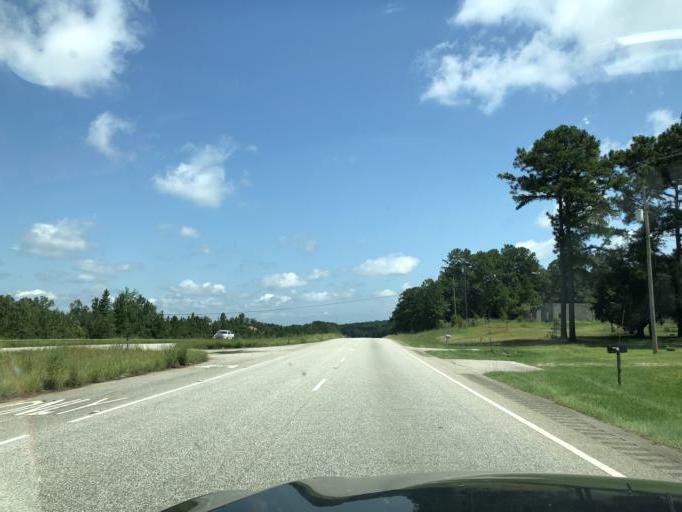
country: US
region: Alabama
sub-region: Henry County
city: Abbeville
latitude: 31.7241
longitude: -85.2626
